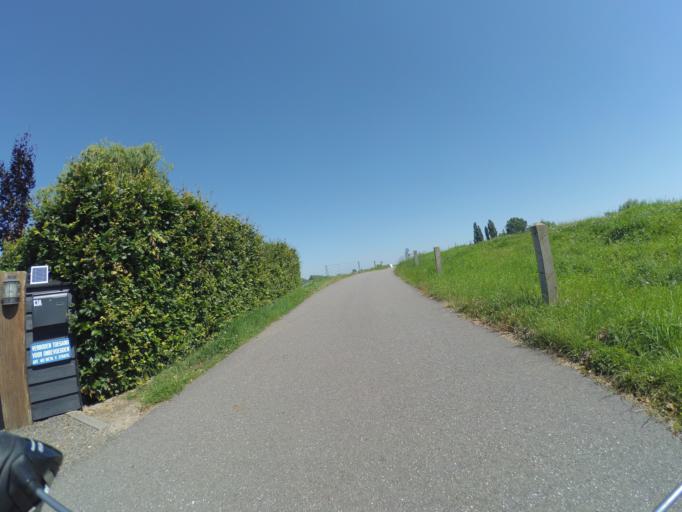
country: NL
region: North Brabant
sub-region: Gemeente Geertruidenberg
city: Geertruidenberg
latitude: 51.7146
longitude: 4.9004
